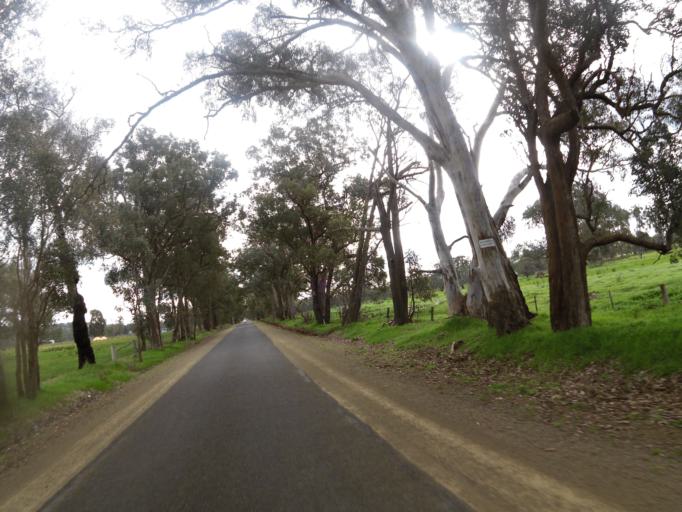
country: AU
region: Victoria
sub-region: Benalla
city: Benalla
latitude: -36.6796
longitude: 145.9678
